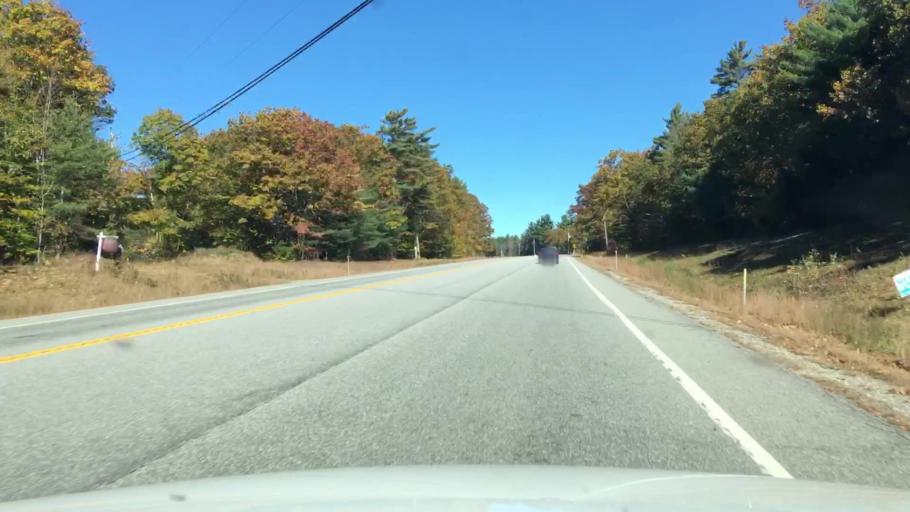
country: US
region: New Hampshire
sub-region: Carroll County
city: Wakefield
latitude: 43.5934
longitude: -71.0318
